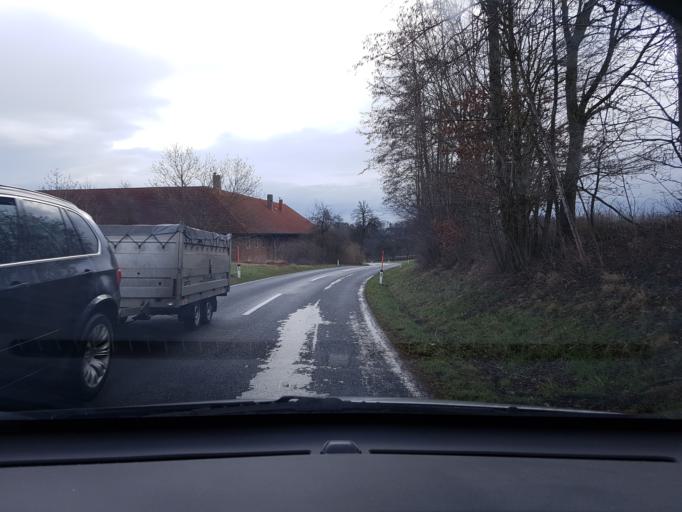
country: AT
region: Upper Austria
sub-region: Politischer Bezirk Linz-Land
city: Sankt Florian
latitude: 48.1508
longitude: 14.3696
